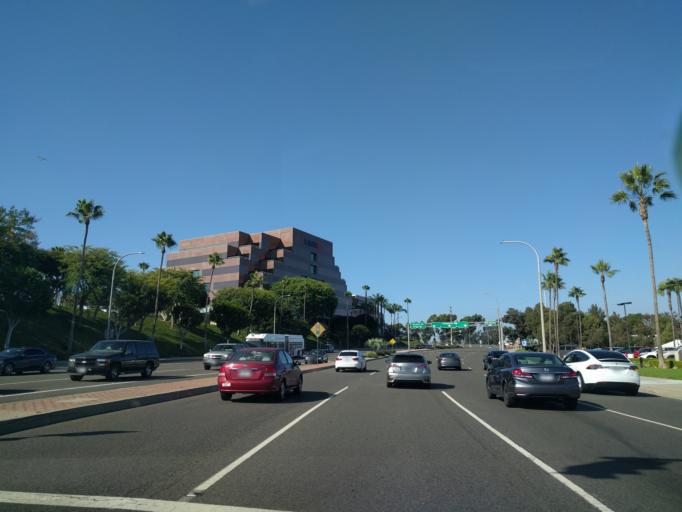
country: US
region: California
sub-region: Orange County
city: Irvine
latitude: 33.6530
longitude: -117.8666
